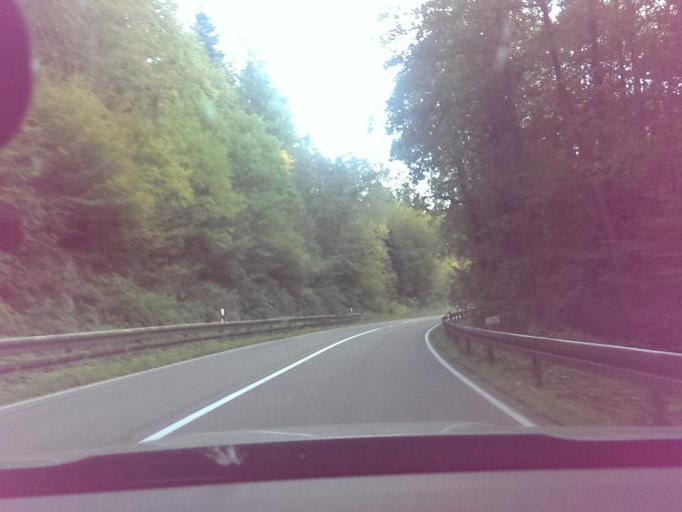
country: DE
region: Baden-Wuerttemberg
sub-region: Karlsruhe Region
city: Pforzheim
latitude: 48.8692
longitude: 8.7143
